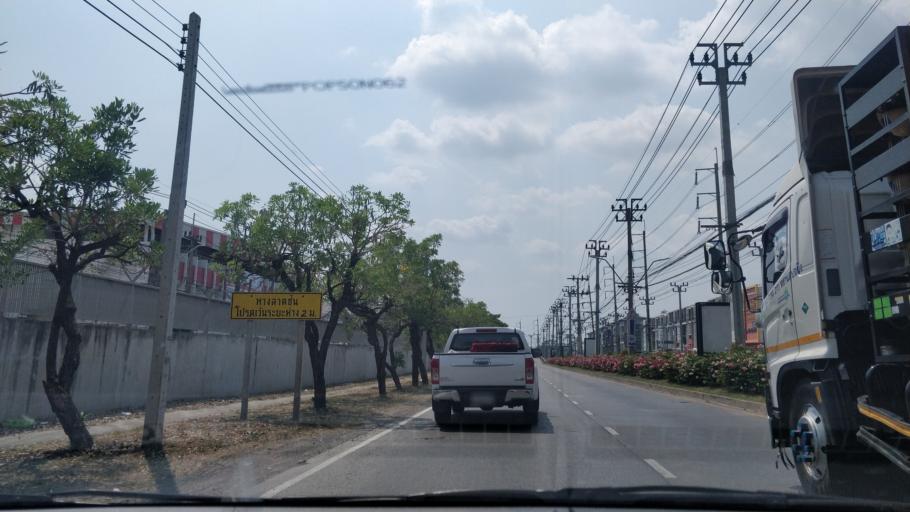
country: TH
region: Bangkok
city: Lat Krabang
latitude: 13.7566
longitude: 100.7949
